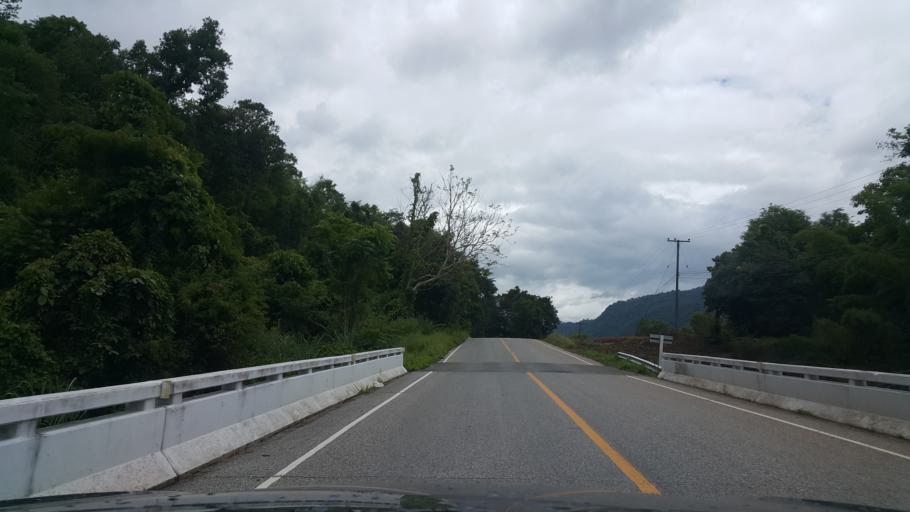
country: TH
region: Phitsanulok
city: Chat Trakan
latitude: 17.3438
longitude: 100.7156
